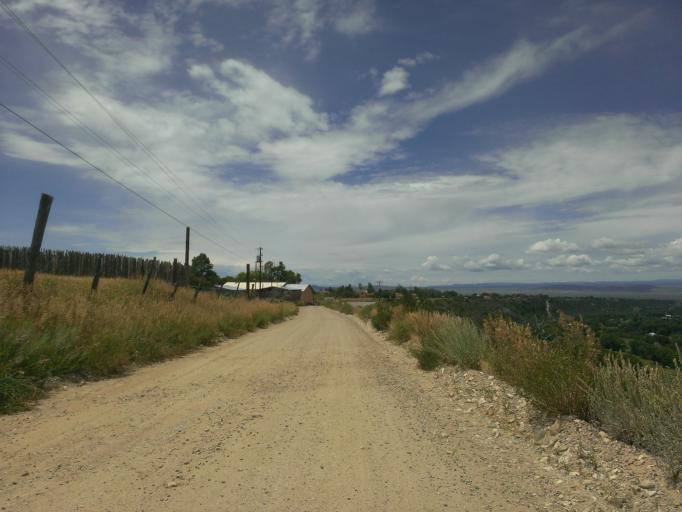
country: US
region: New Mexico
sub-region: Taos County
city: Arroyo Seco
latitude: 36.5339
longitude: -105.5649
